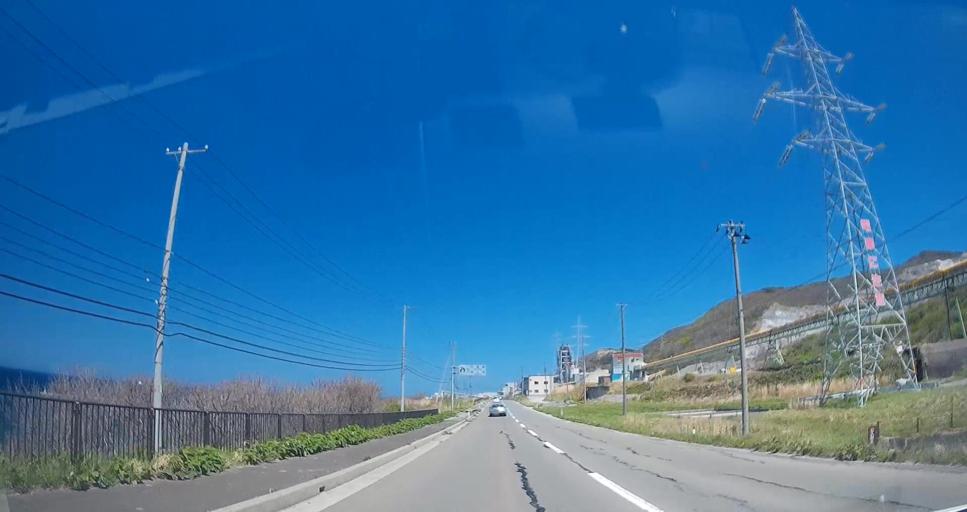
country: JP
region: Aomori
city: Mutsu
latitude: 41.4017
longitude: 141.4274
